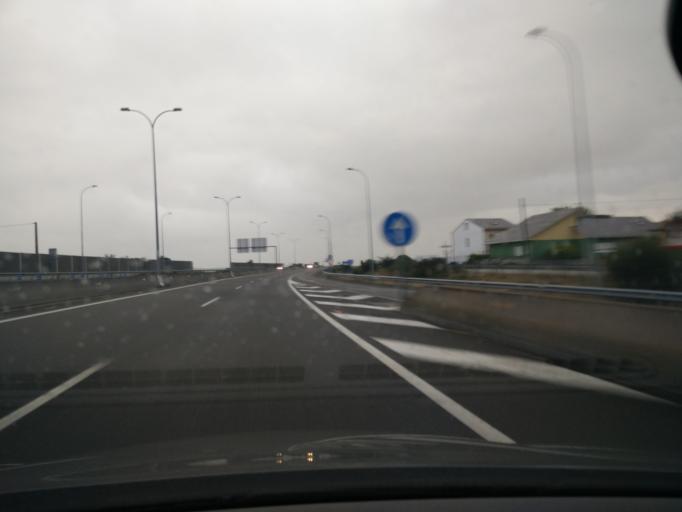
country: ES
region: Galicia
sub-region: Provincia de Lugo
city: Ribadeo
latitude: 43.5425
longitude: -7.0446
